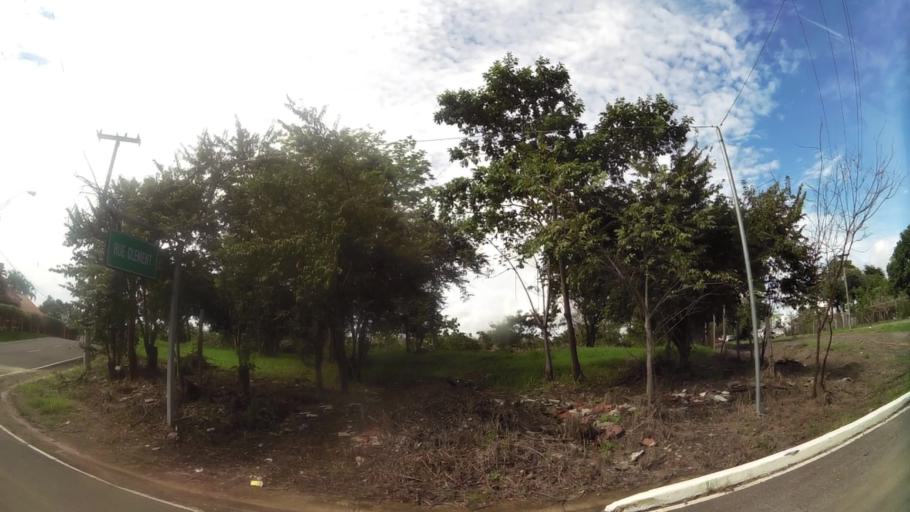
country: PA
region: Panama
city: Nueva Gorgona
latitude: 8.5474
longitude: -79.8787
